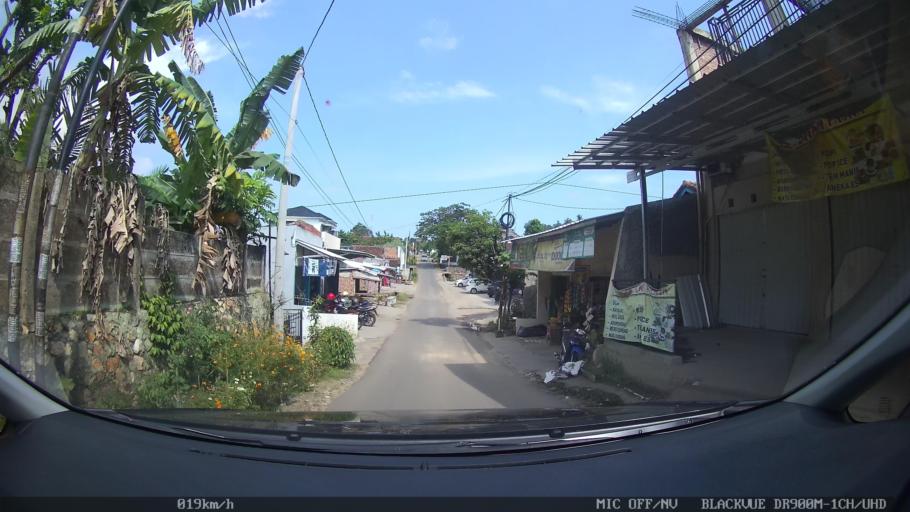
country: ID
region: Lampung
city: Kedaton
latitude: -5.4002
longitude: 105.2308
